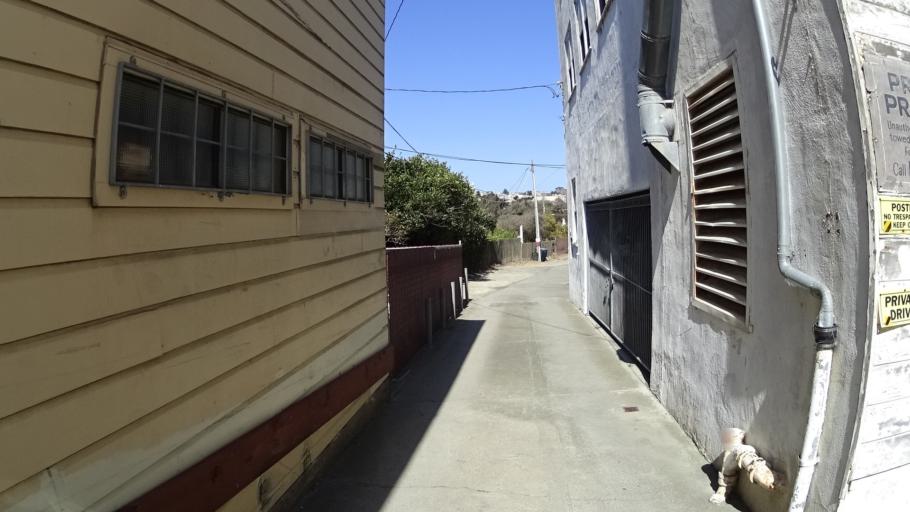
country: US
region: California
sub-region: San Mateo County
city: Daly City
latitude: 37.7302
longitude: -122.4304
